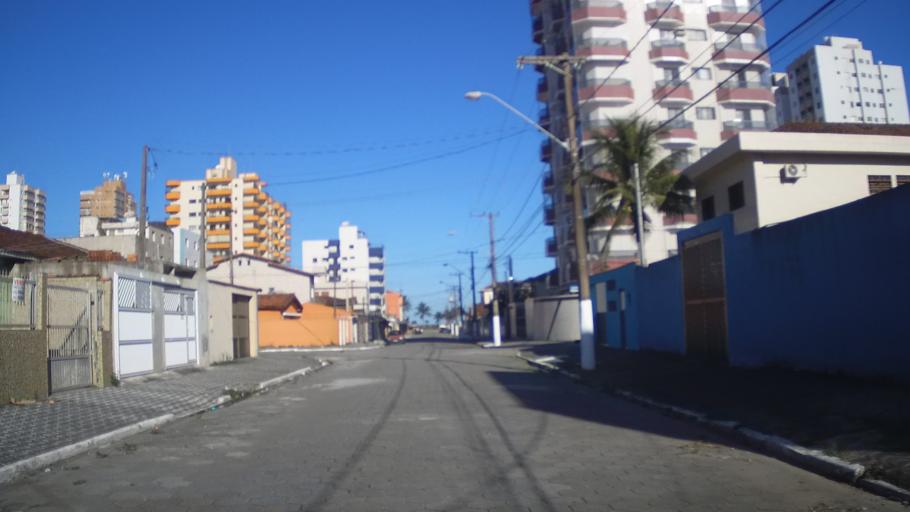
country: BR
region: Sao Paulo
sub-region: Praia Grande
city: Praia Grande
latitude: -24.0298
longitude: -46.4810
